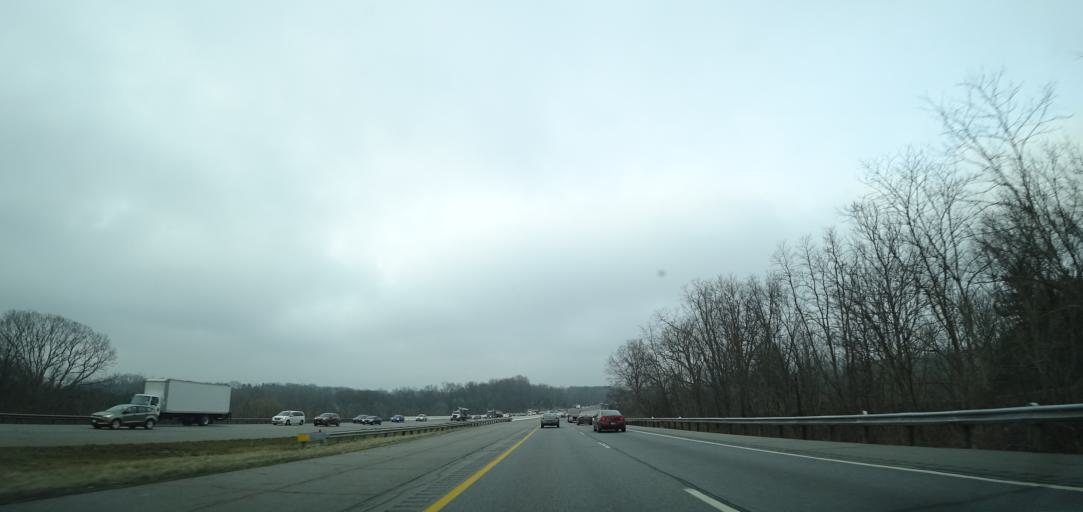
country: US
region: Ohio
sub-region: Summit County
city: Montrose-Ghent
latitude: 41.1587
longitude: -81.6264
